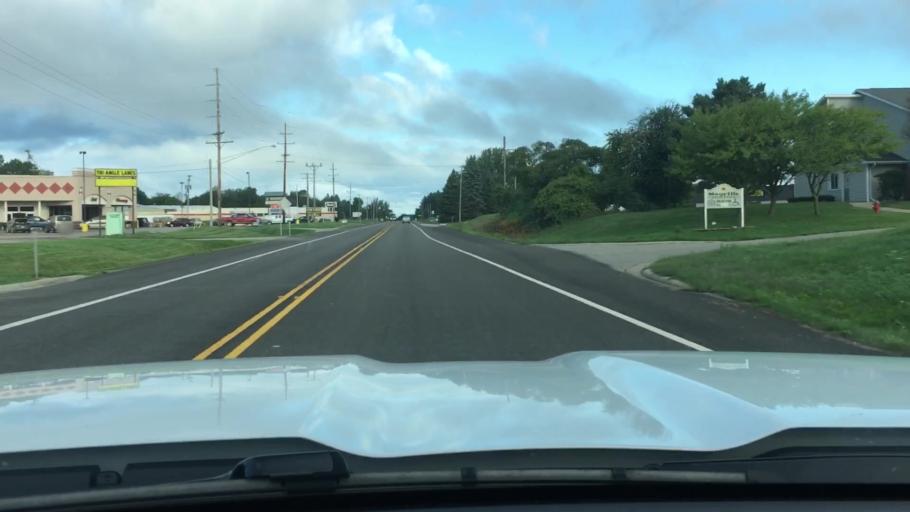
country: US
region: Michigan
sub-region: Lapeer County
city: Barnes Lake-Millers Lake
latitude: 43.3375
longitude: -83.3461
